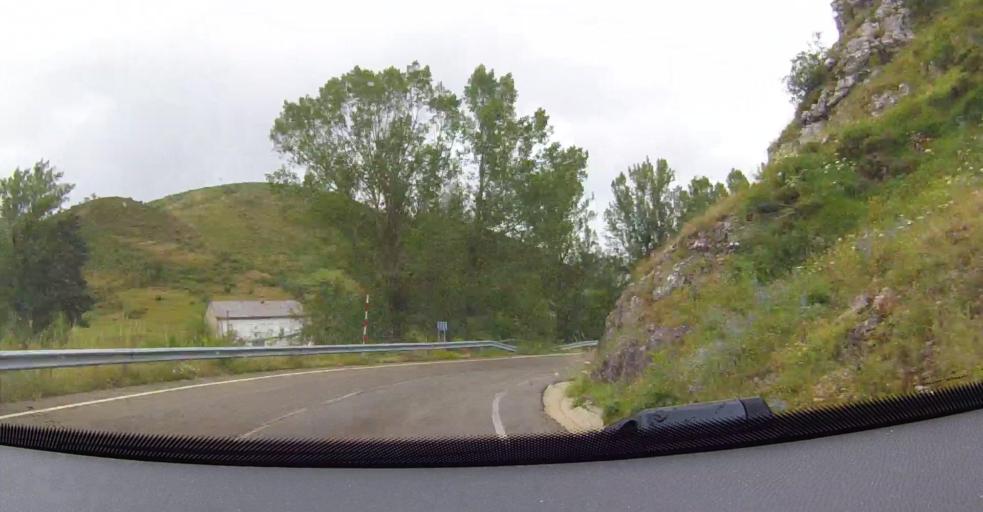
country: ES
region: Castille and Leon
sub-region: Provincia de Leon
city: Acebedo
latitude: 43.0661
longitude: -5.1374
